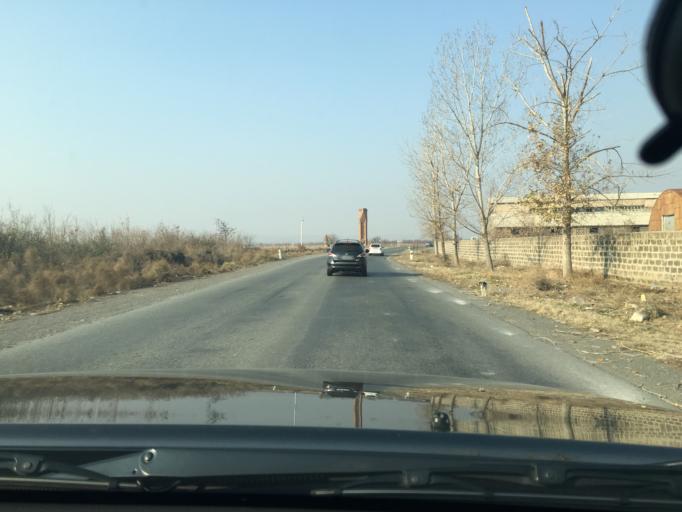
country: AM
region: Armavir
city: Myasnikyan
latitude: 40.1761
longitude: 43.9408
